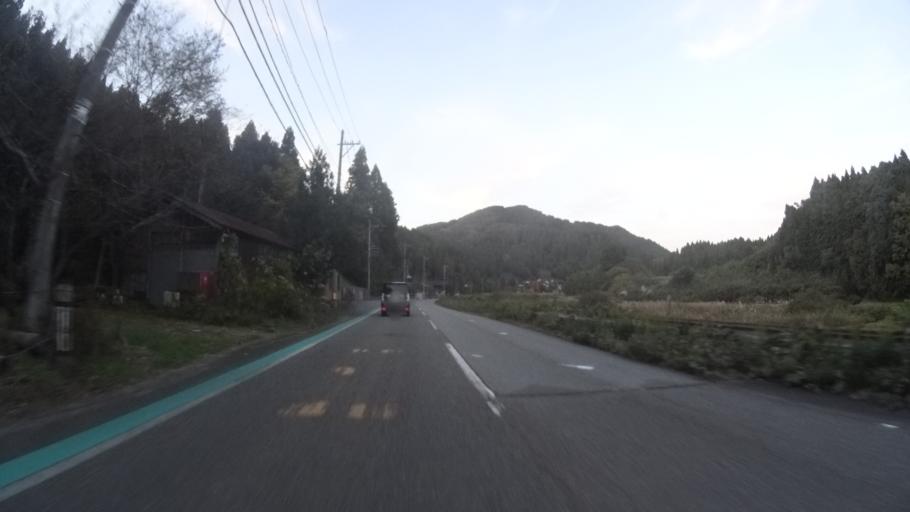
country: JP
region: Ishikawa
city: Nanao
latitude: 37.3096
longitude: 136.7983
